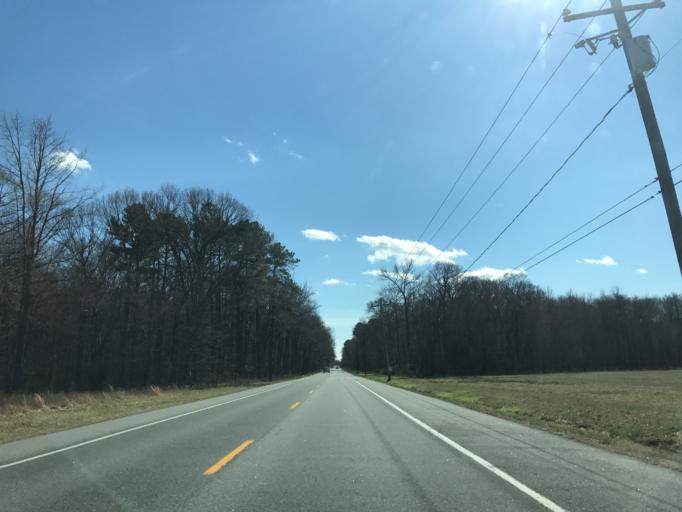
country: US
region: Maryland
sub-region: Kent County
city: Rock Hall
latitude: 39.1954
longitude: -76.1908
